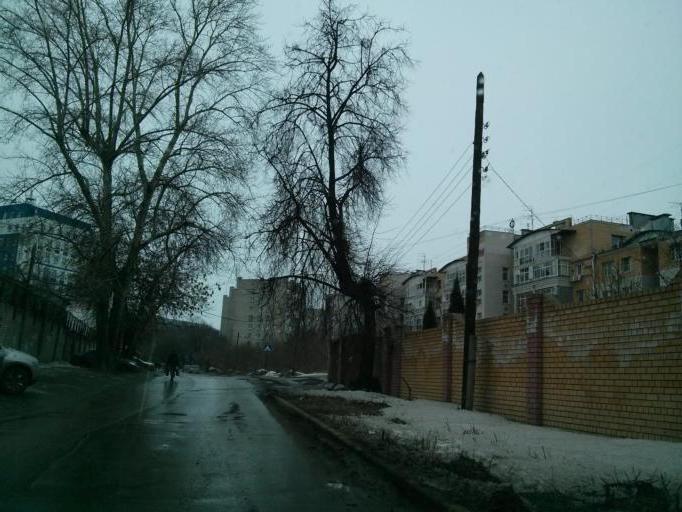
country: RU
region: Nizjnij Novgorod
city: Nizhniy Novgorod
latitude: 56.3182
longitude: 44.0429
